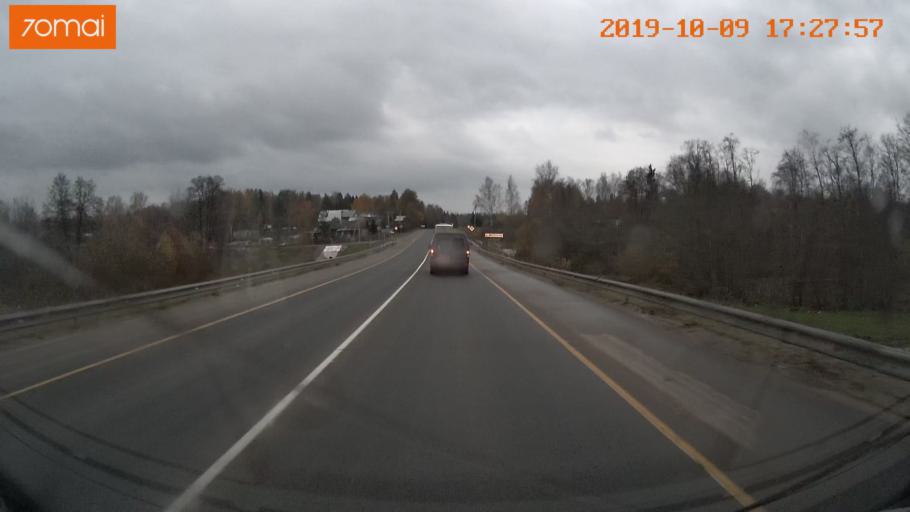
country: RU
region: Ivanovo
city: Furmanov
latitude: 57.1622
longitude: 41.0692
